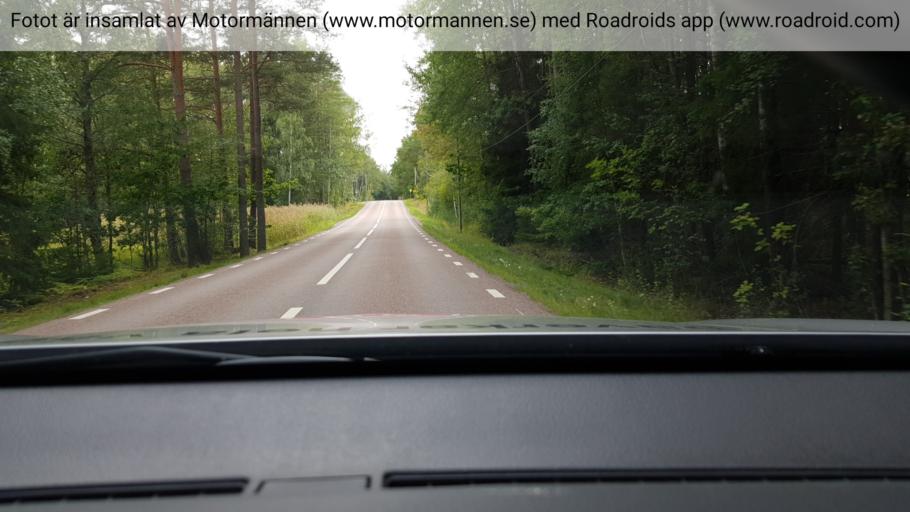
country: SE
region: Soedermanland
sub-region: Nykopings Kommun
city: Nykoping
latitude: 58.9336
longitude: 17.1128
